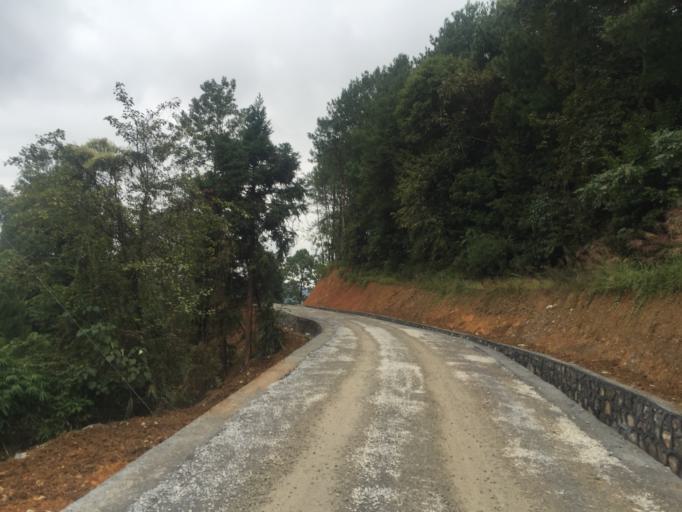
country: CN
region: Guizhou Sheng
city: Zhongba
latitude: 27.9773
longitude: 108.2200
